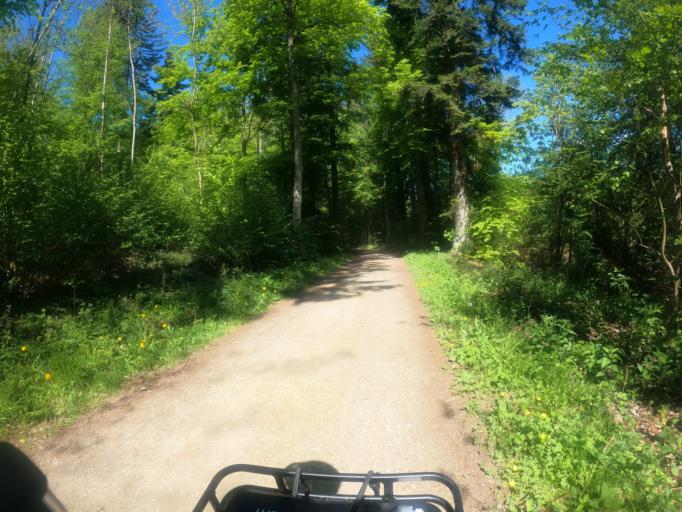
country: CH
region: Zurich
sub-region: Bezirk Affoltern
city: Affoltern / Sonnenberg
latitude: 47.2817
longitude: 8.4652
